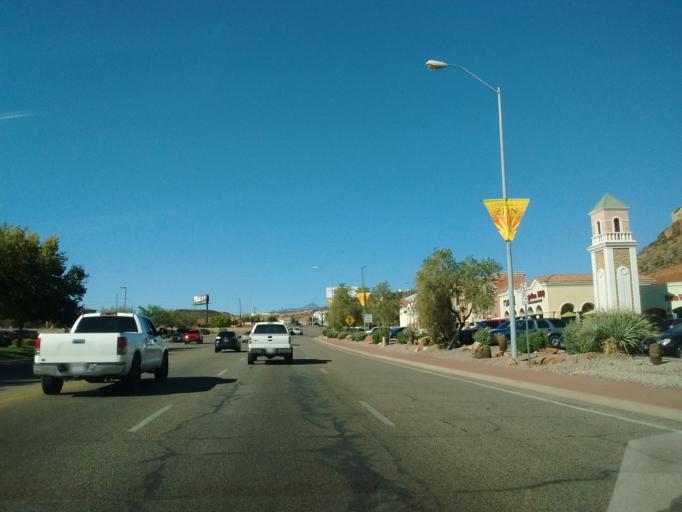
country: US
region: Utah
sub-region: Washington County
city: Saint George
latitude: 37.1124
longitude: -113.5540
